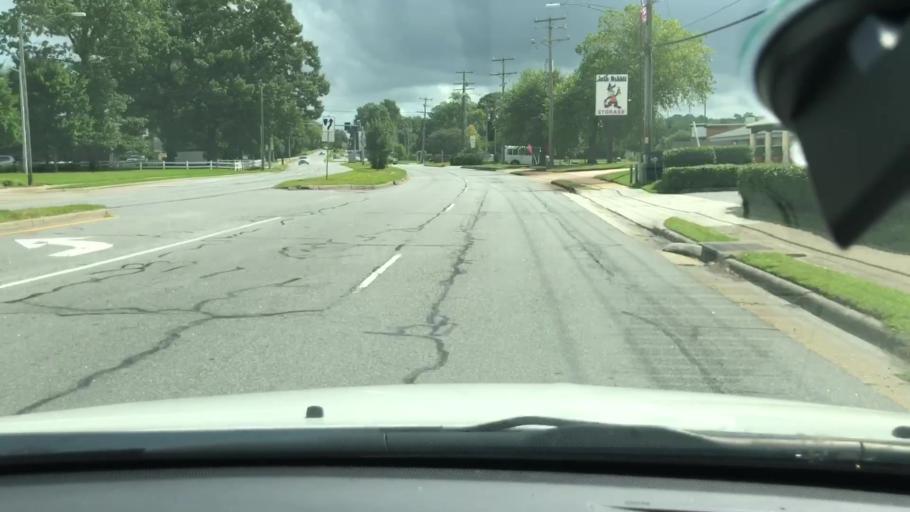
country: US
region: Virginia
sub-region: City of Chesapeake
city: Chesapeake
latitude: 36.8126
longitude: -76.2010
